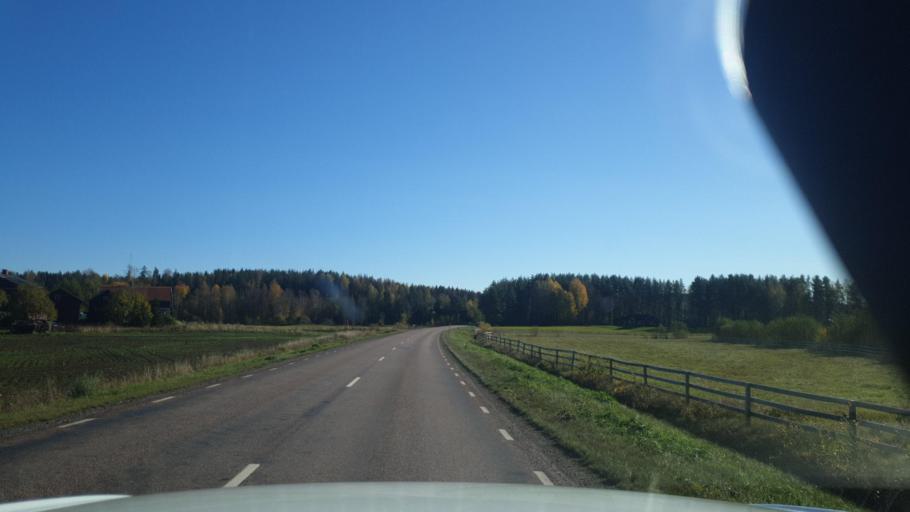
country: SE
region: Vaermland
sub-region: Grums Kommun
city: Slottsbron
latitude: 59.4117
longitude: 12.9966
